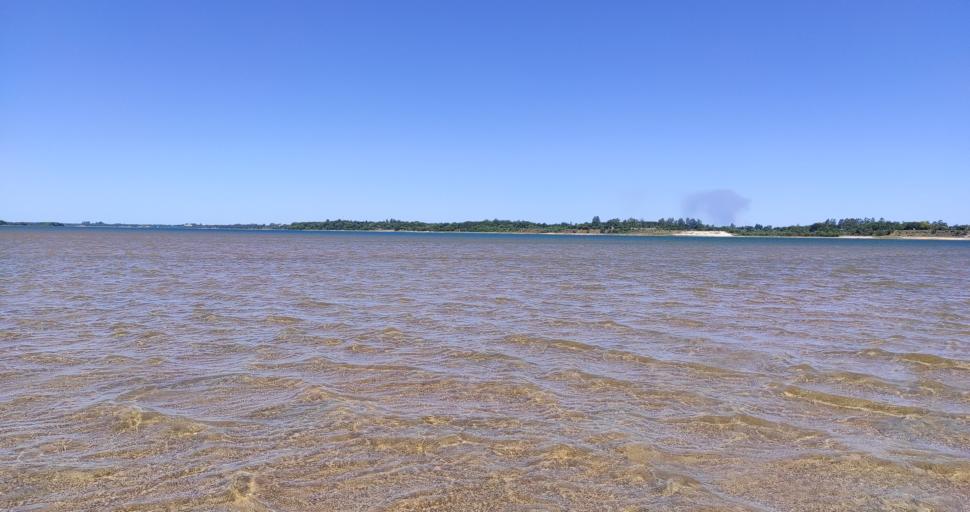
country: AR
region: Corrientes
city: Ituzaingo
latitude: -27.5954
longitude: -56.7348
